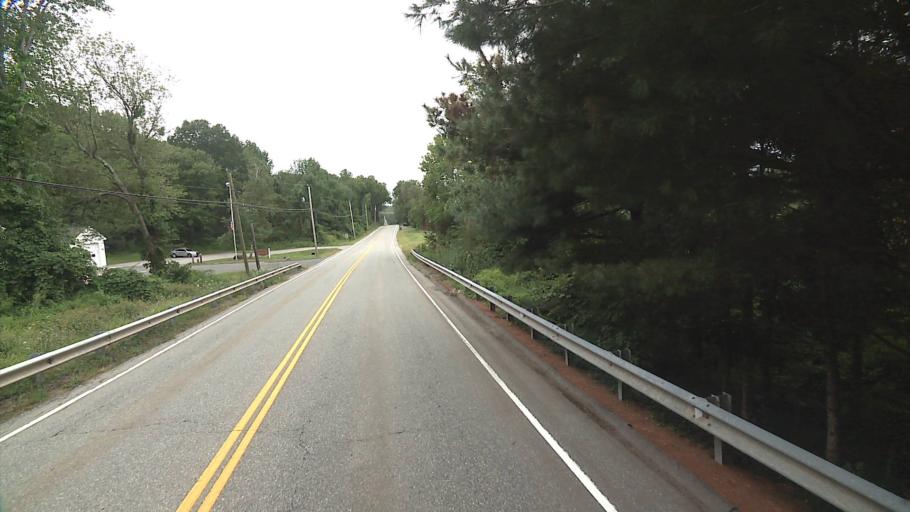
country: US
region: Connecticut
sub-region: Hartford County
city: Terramuggus
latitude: 41.7034
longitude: -72.4345
